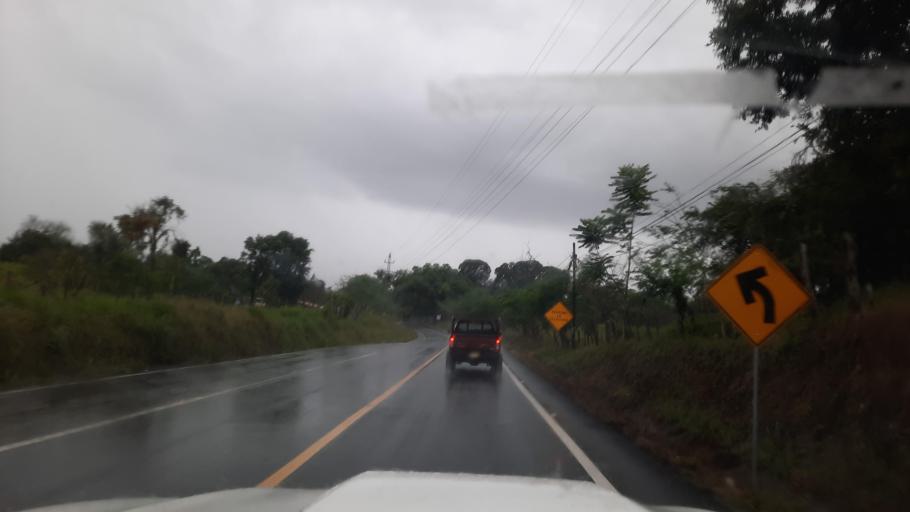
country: PA
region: Chiriqui
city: Sortova
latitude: 8.5609
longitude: -82.6278
